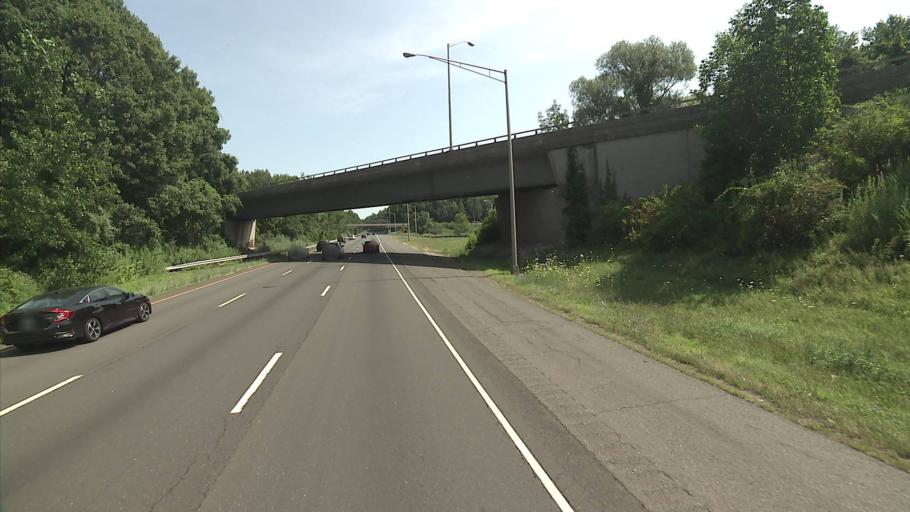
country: US
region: Connecticut
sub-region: Middlesex County
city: Cromwell
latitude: 41.6215
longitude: -72.6926
